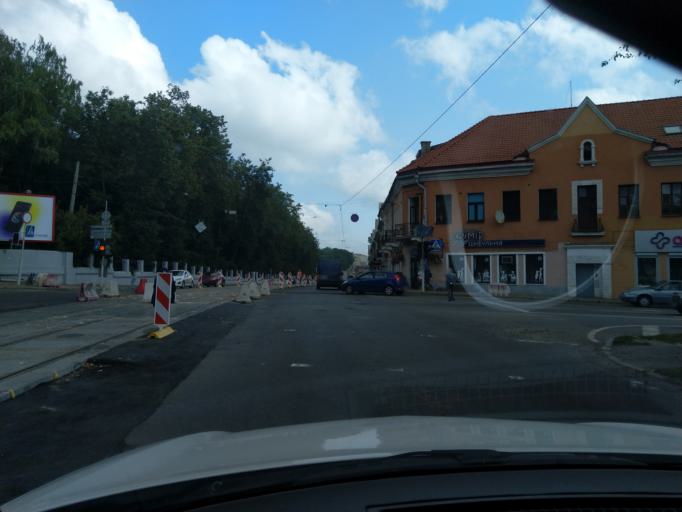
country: BY
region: Minsk
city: Minsk
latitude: 53.8979
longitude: 27.5693
